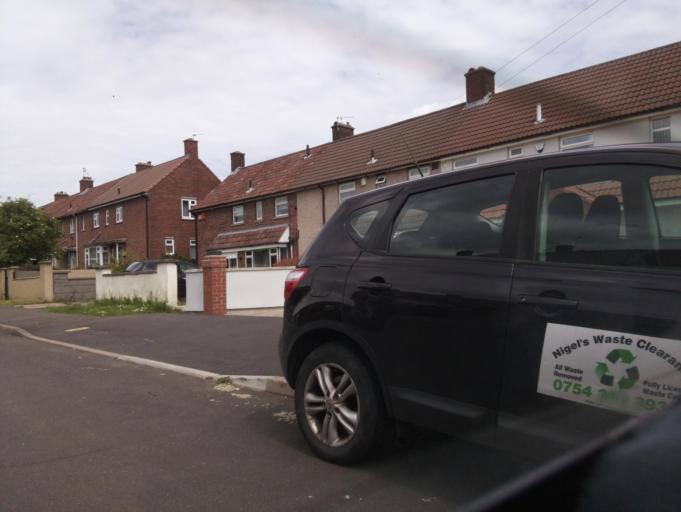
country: GB
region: England
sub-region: Bristol
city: Bristol
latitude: 51.5032
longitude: -2.6094
